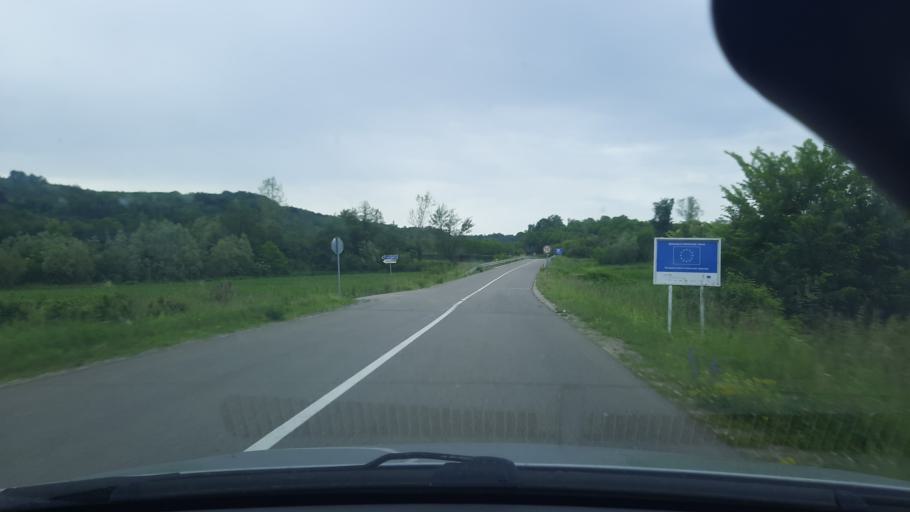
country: RS
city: Bukor
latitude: 44.5277
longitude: 19.5146
